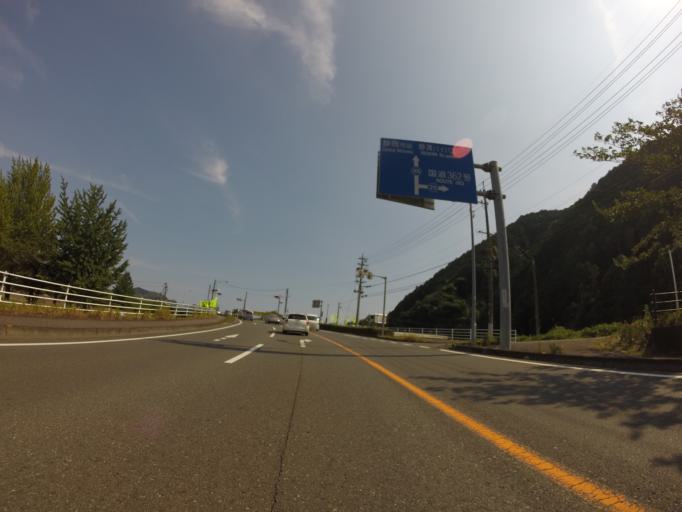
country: JP
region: Shizuoka
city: Shizuoka-shi
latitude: 35.0097
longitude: 138.3553
